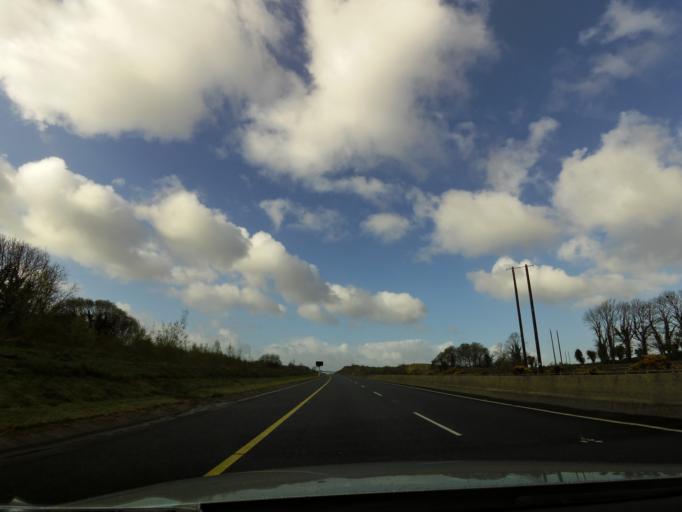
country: IE
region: Munster
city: Ballina
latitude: 52.7789
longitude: -8.3756
